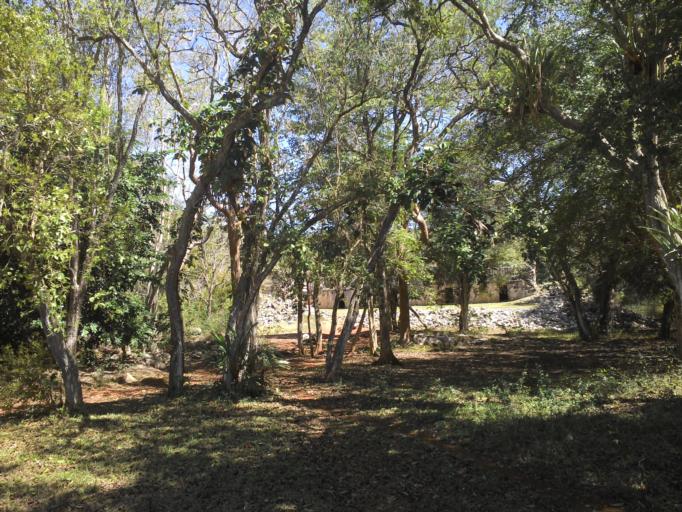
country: MX
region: Yucatan
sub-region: Oxkutzcab
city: Xul
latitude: 20.1722
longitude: -89.5781
